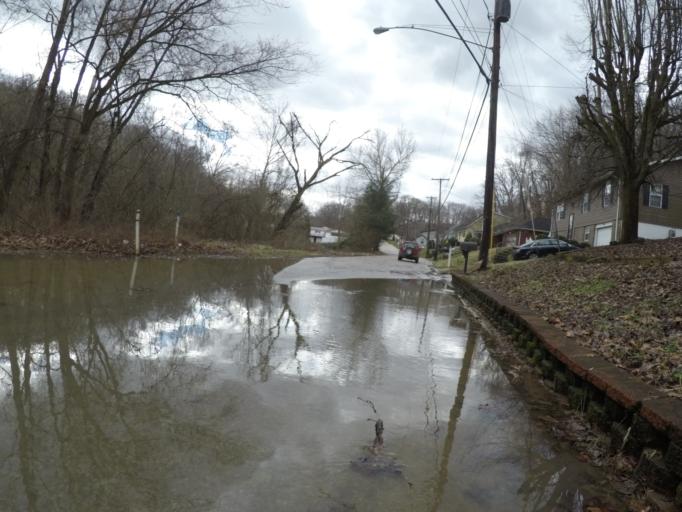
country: US
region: West Virginia
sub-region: Cabell County
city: Pea Ridge
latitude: 38.4096
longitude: -82.3828
